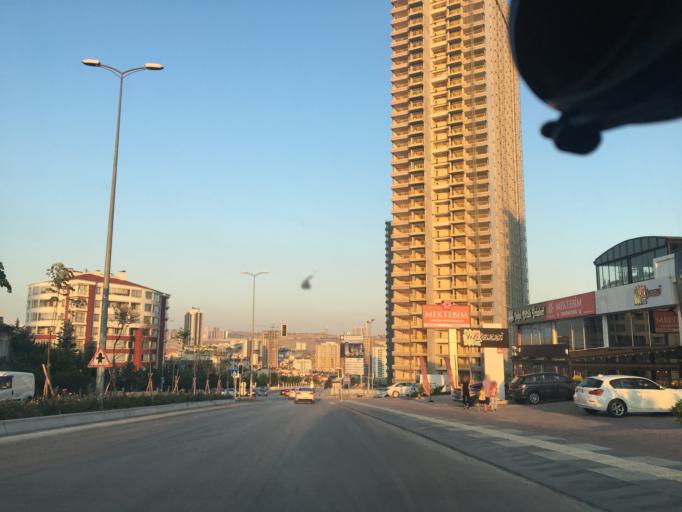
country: TR
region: Ankara
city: Etimesgut
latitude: 39.8570
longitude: 32.6509
